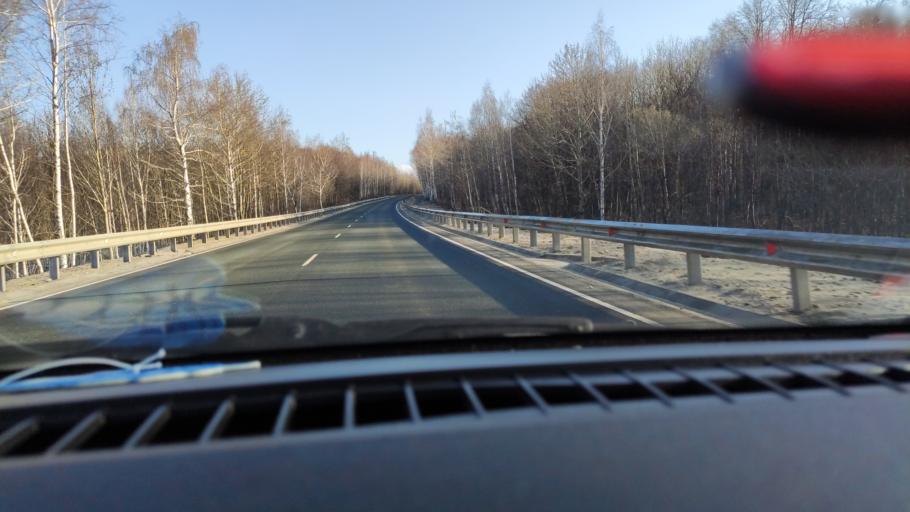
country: RU
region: Saratov
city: Khvalynsk
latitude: 52.4453
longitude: 48.0100
